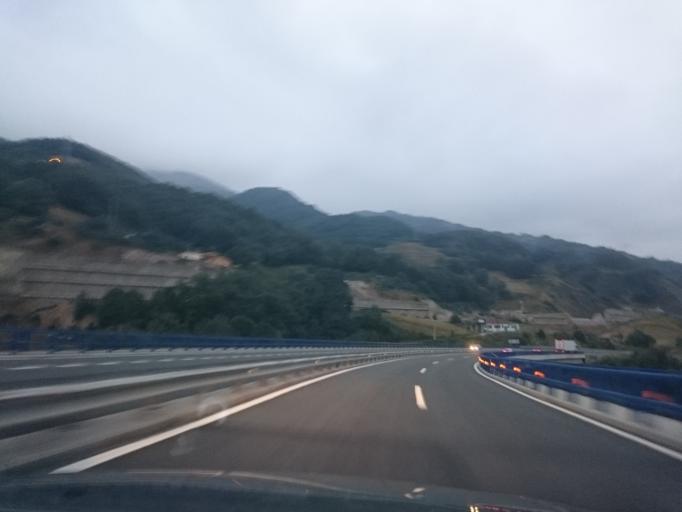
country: ES
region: Asturias
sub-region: Province of Asturias
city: Pola de Lena
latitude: 43.1043
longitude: -5.8207
